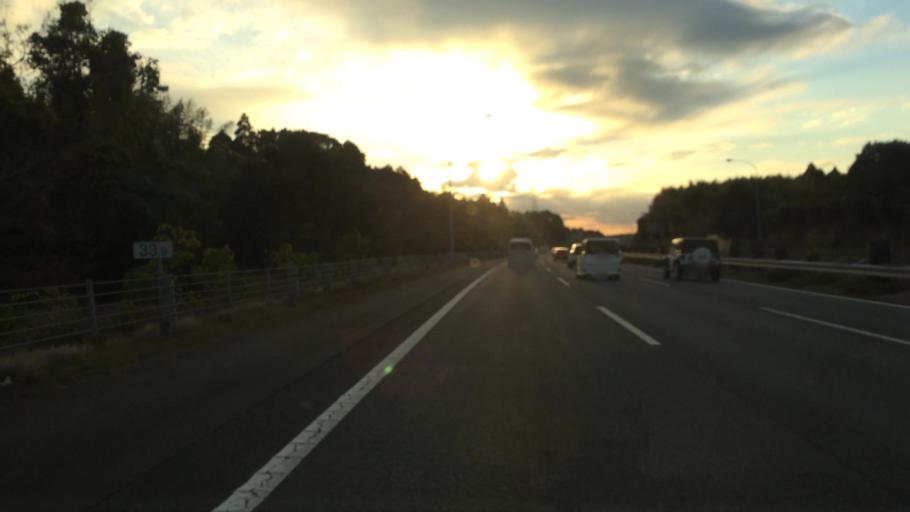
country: JP
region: Chiba
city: Shisui
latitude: 35.7036
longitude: 140.2753
